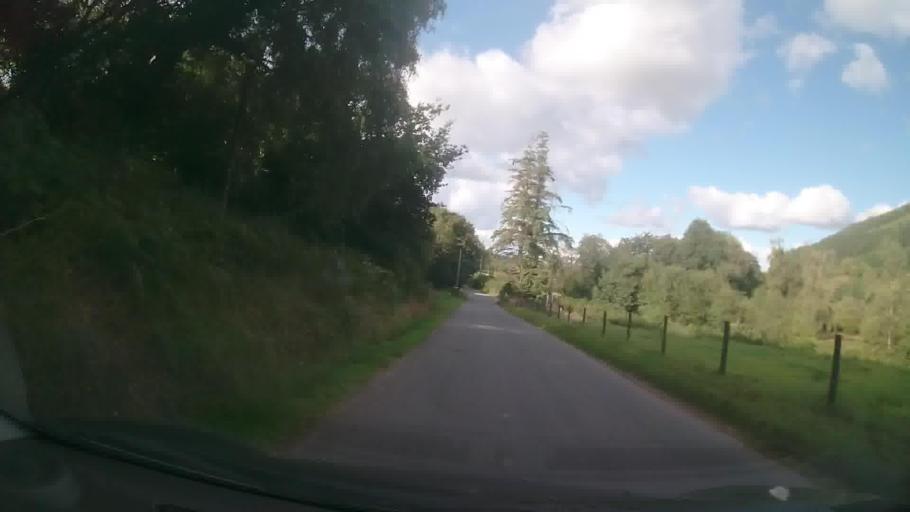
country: GB
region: Wales
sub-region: Sir Powys
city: Brecon
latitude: 51.8794
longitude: -3.3015
